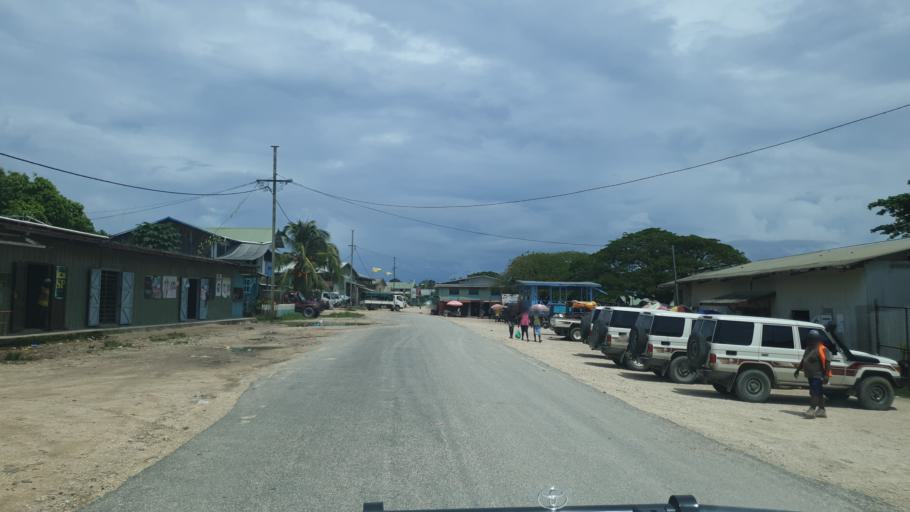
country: PG
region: Bougainville
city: Buka
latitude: -5.4343
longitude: 154.6752
